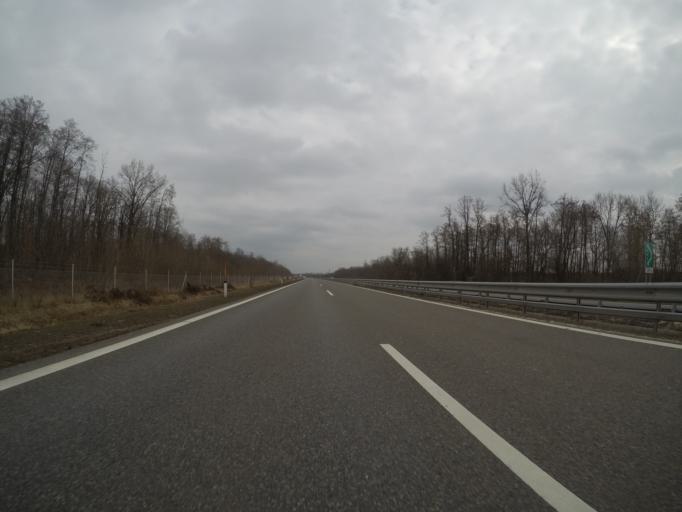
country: SI
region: Turnisce
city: Turnisce
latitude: 46.6063
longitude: 16.3268
